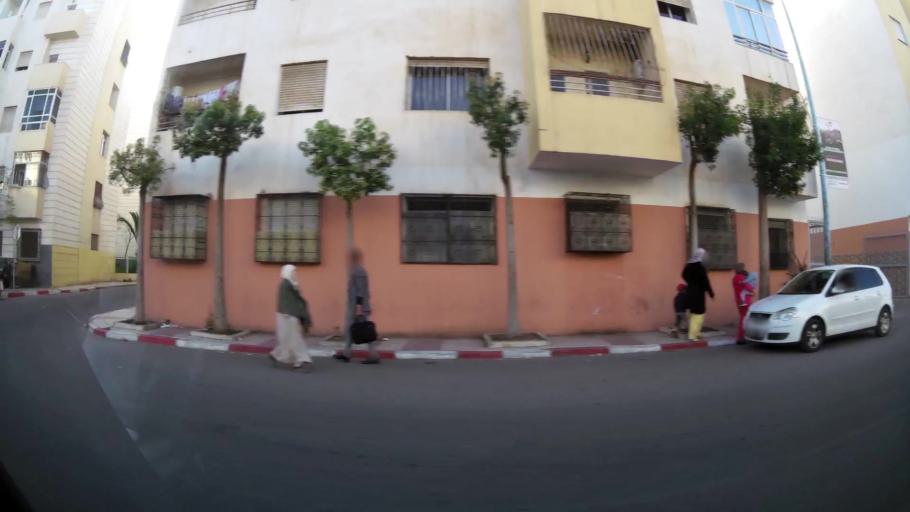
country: MA
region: Oued ed Dahab-Lagouira
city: Dakhla
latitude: 30.3956
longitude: -9.5479
